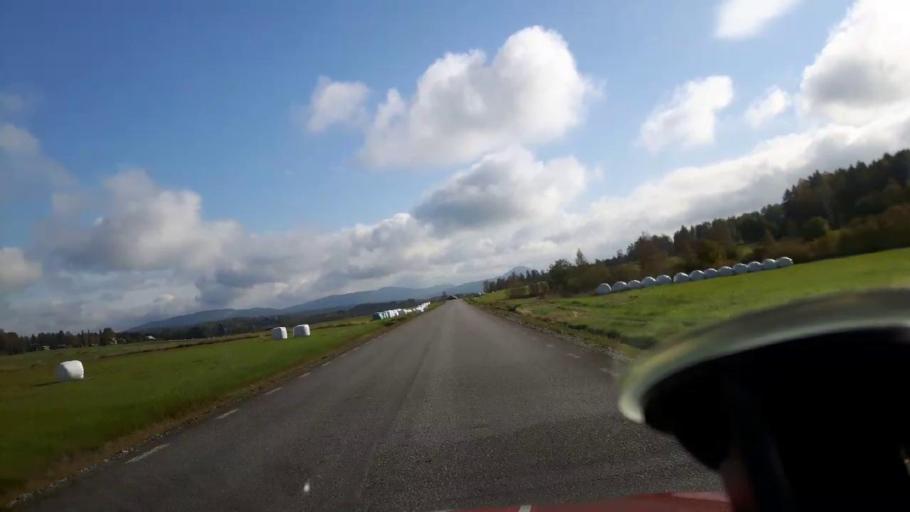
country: SE
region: Gaevleborg
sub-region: Ljusdals Kommun
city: Ljusdal
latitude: 61.7632
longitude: 16.0670
